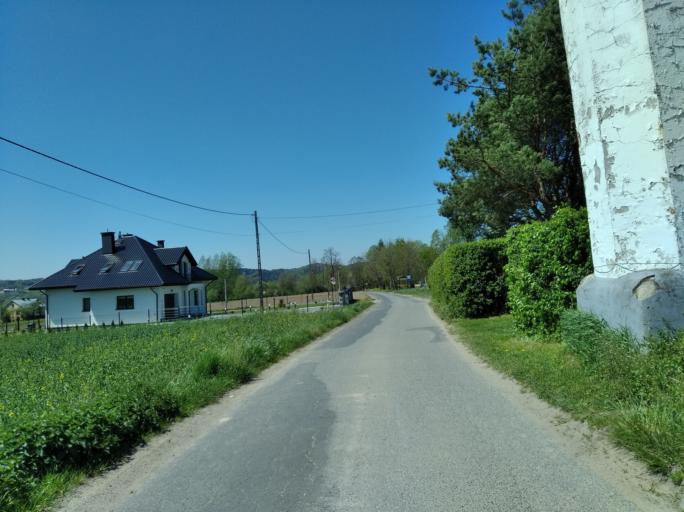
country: PL
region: Subcarpathian Voivodeship
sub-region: Powiat debicki
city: Brzostek
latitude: 49.8938
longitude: 21.3921
